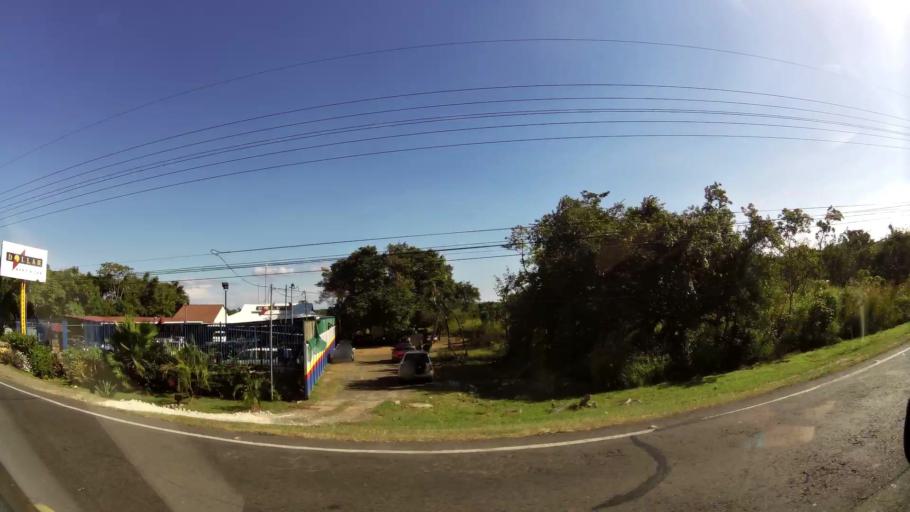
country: CR
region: Guanacaste
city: Liberia
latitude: 10.6034
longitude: -85.5136
